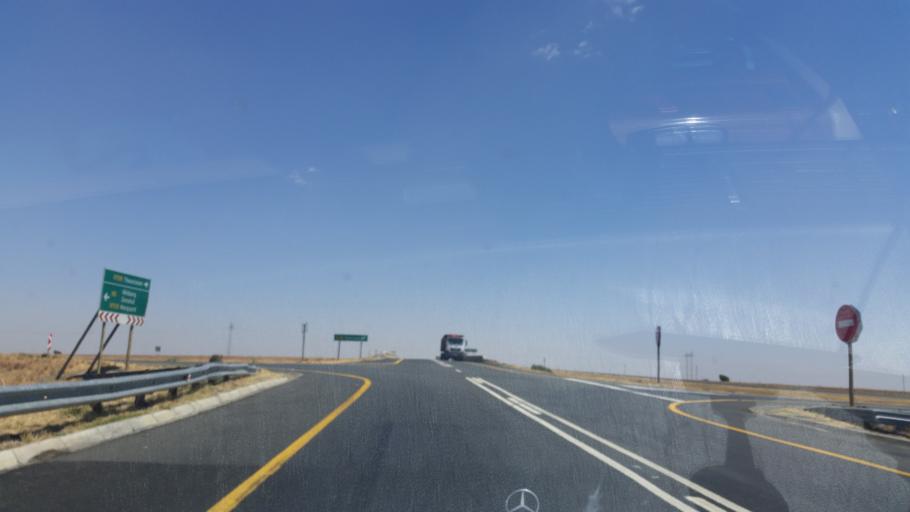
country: ZA
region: Orange Free State
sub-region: Lejweleputswa District Municipality
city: Winburg
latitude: -28.4990
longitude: 26.9984
